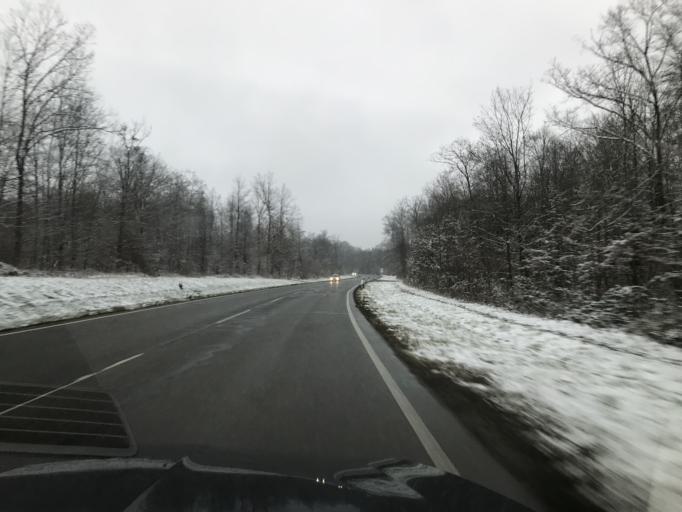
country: DE
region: Baden-Wuerttemberg
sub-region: Regierungsbezirk Stuttgart
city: Altbach
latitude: 48.7368
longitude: 9.3959
